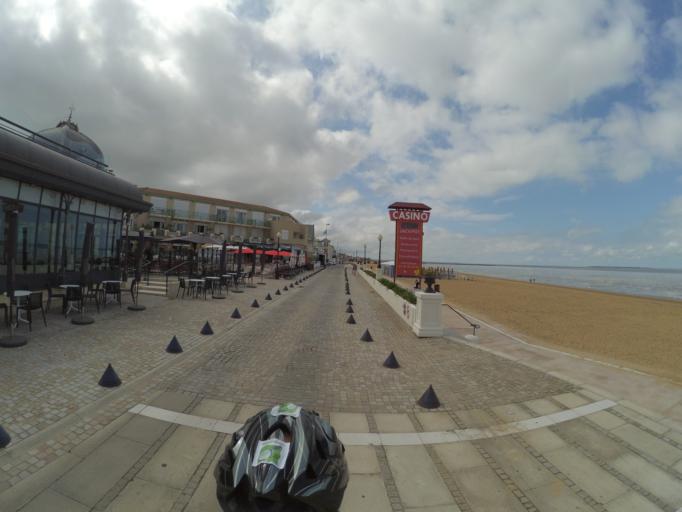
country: FR
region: Poitou-Charentes
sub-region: Departement de la Charente-Maritime
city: Chatelaillon-Plage
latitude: 46.0764
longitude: -1.0939
